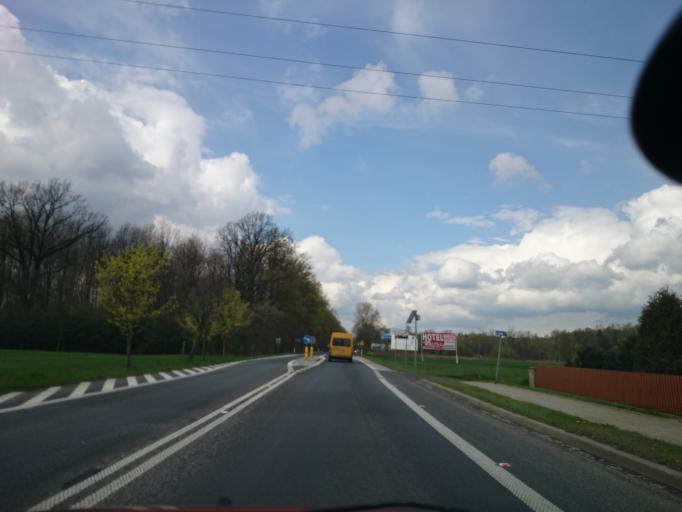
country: PL
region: Opole Voivodeship
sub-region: Powiat opolski
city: Naklo
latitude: 50.5868
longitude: 18.1041
